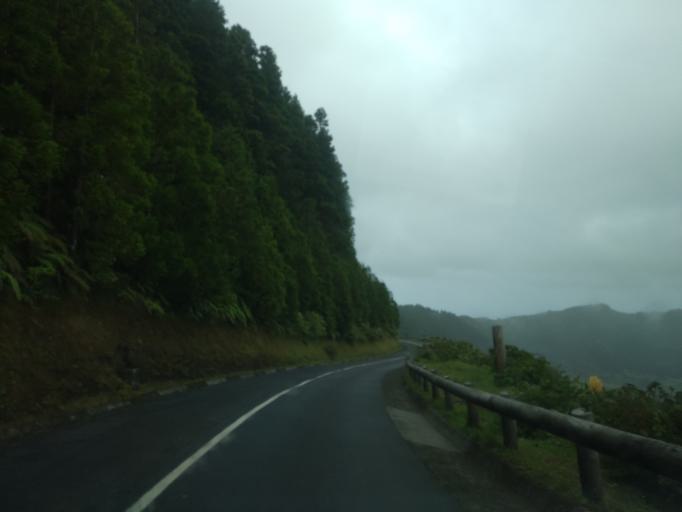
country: PT
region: Azores
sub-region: Ponta Delgada
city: Arrifes
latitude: 37.8389
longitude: -25.7904
